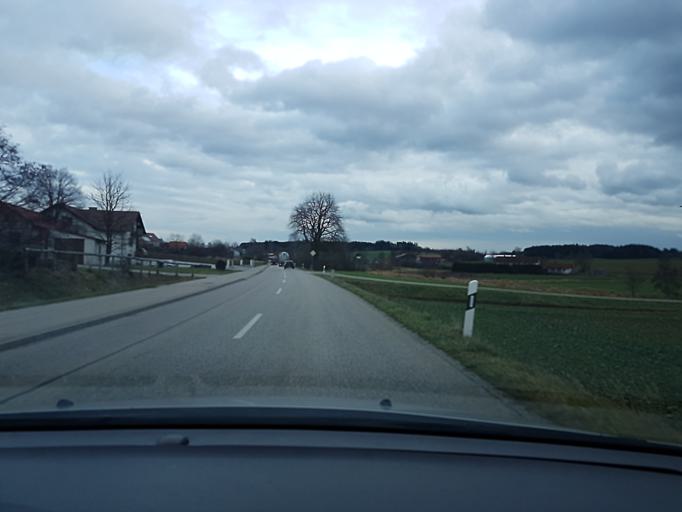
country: DE
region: Bavaria
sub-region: Lower Bavaria
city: Furth
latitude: 48.4043
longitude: 12.3854
